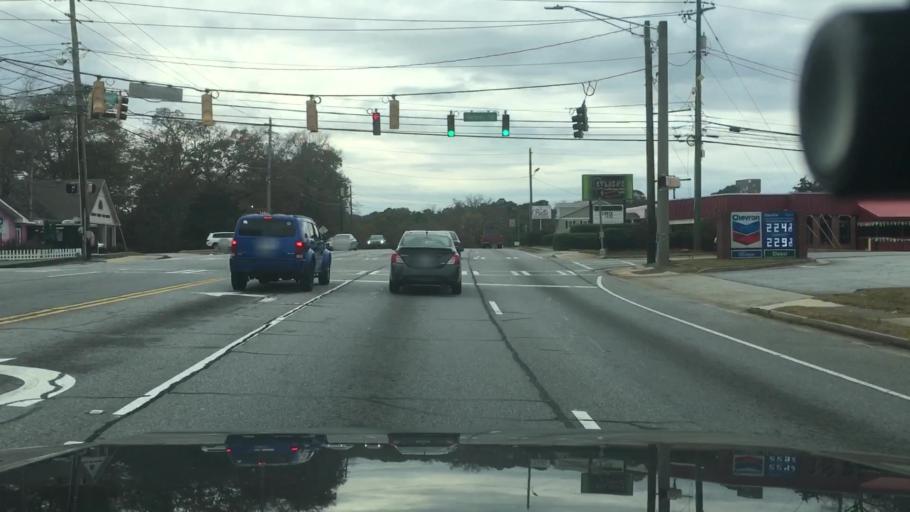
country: US
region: Georgia
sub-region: Coweta County
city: Newnan
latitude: 33.3827
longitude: -84.7907
